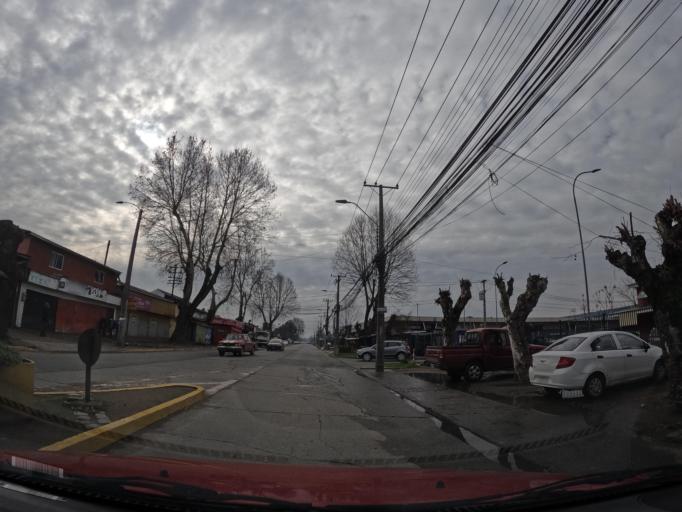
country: CL
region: Maule
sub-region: Provincia de Linares
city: Linares
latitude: -35.8470
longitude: -71.5894
